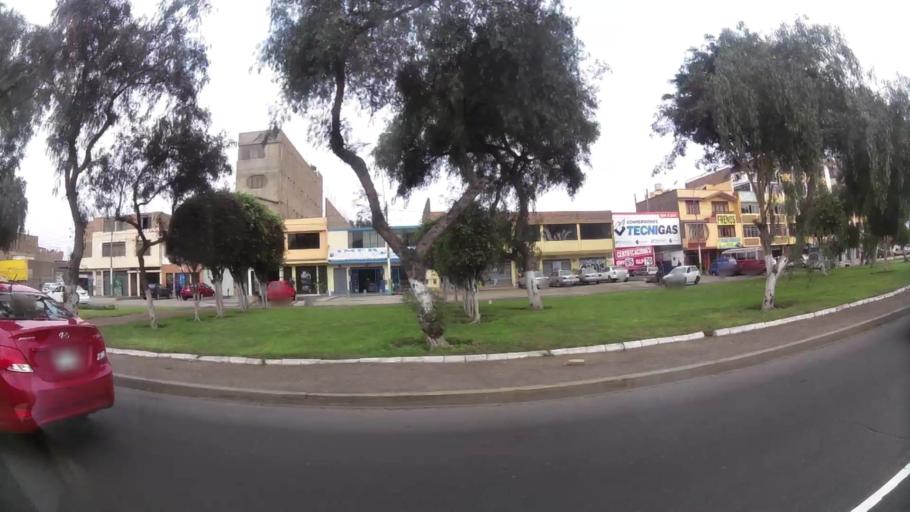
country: PE
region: Callao
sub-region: Callao
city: Callao
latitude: -12.0130
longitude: -77.0940
